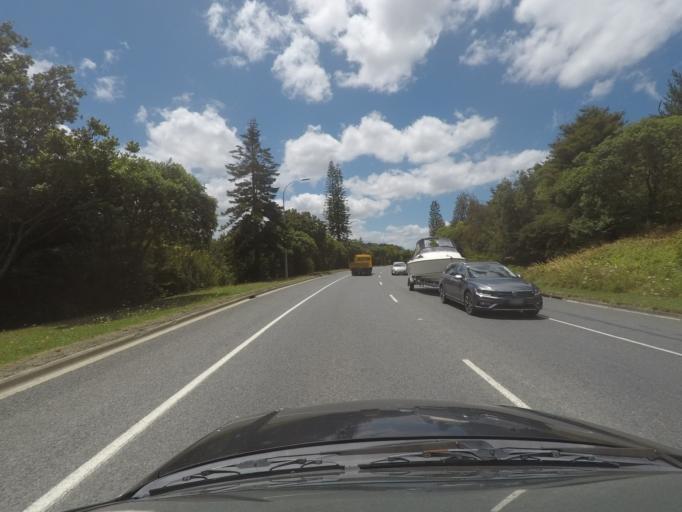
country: NZ
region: Northland
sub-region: Whangarei
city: Whangarei
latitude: -35.7470
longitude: 174.3211
